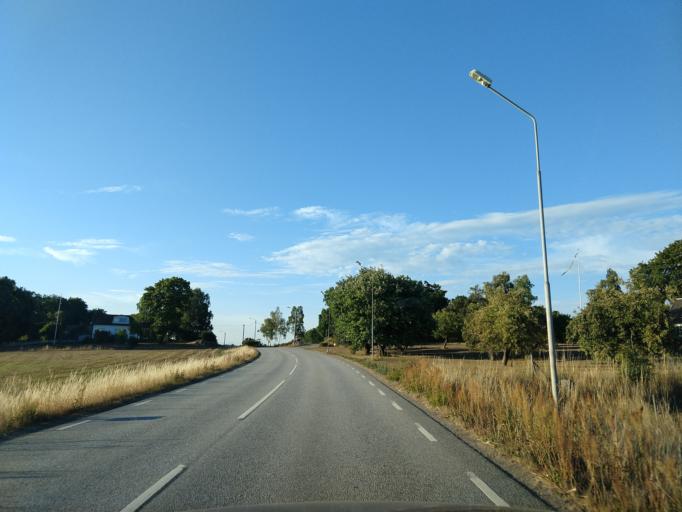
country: SE
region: Blekinge
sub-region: Ronneby Kommun
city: Brakne-Hoby
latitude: 56.2418
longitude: 15.1179
